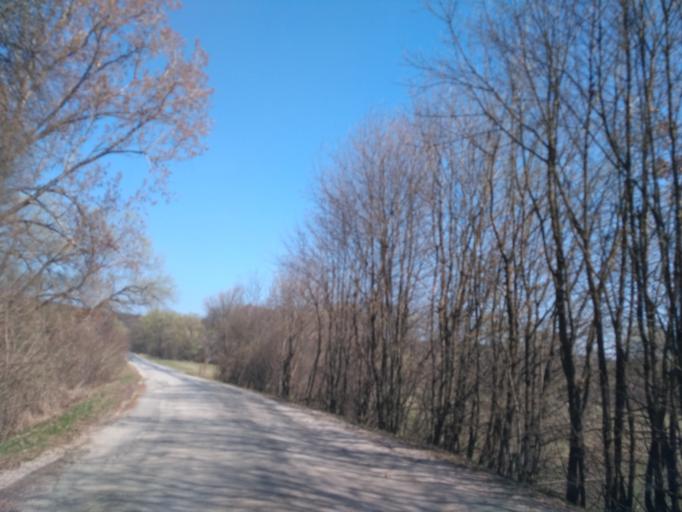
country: SK
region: Kosicky
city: Moldava nad Bodvou
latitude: 48.6460
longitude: 21.0006
